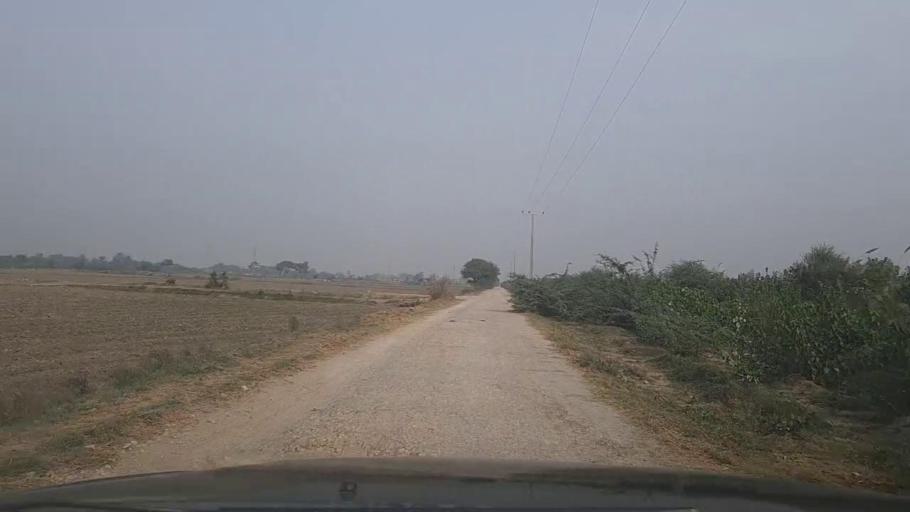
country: PK
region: Sindh
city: Mirpur Sakro
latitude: 24.5660
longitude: 67.7852
